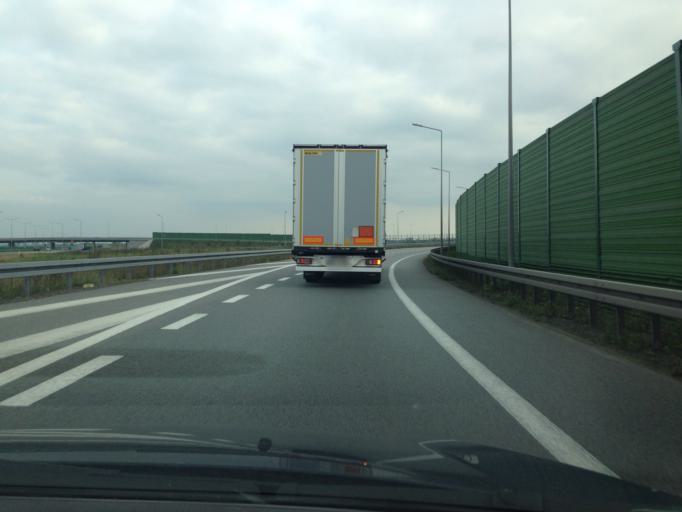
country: PL
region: Greater Poland Voivodeship
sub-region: Powiat poznanski
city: Kleszczewo
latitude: 52.3189
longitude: 17.1232
